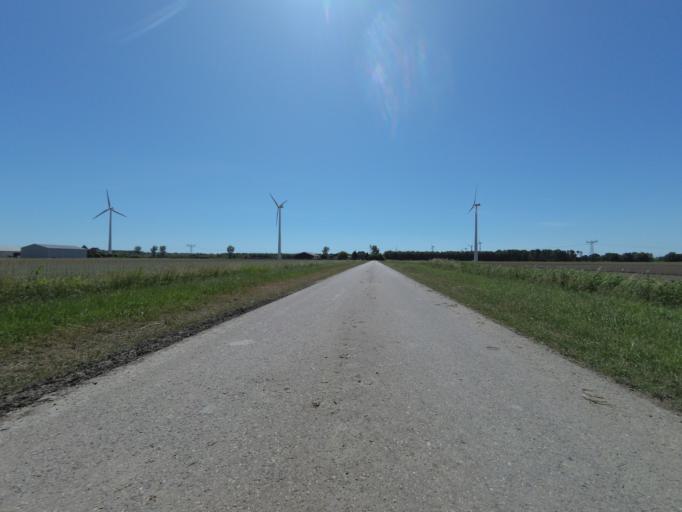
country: NL
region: Utrecht
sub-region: Gemeente Bunschoten
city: Bunschoten
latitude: 52.3362
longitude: 5.4250
